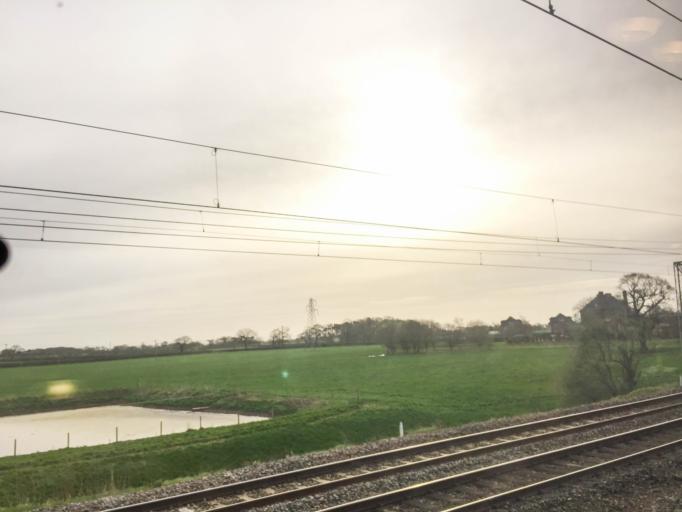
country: GB
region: England
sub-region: Cheshire West and Chester
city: Winsford
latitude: 53.1747
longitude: -2.4819
